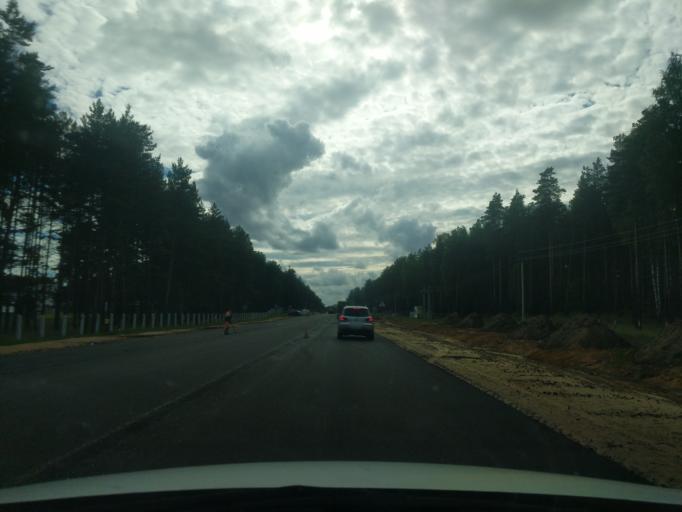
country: RU
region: Jaroslavl
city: Levashevo
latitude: 57.6789
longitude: 40.5929
